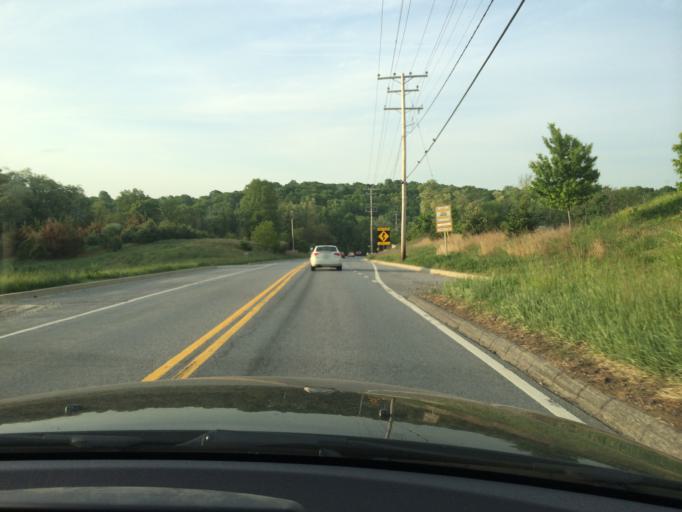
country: US
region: Maryland
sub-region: Carroll County
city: Sykesville
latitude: 39.3564
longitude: -77.0167
